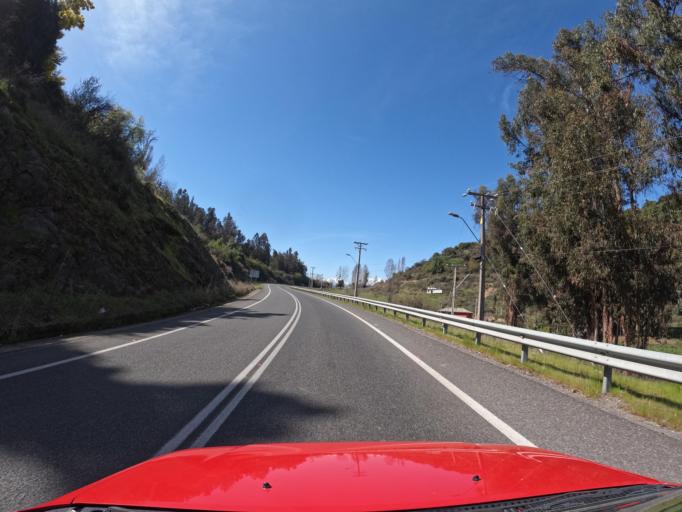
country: CL
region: Maule
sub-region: Provincia de Curico
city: Teno
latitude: -34.9784
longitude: -70.9685
